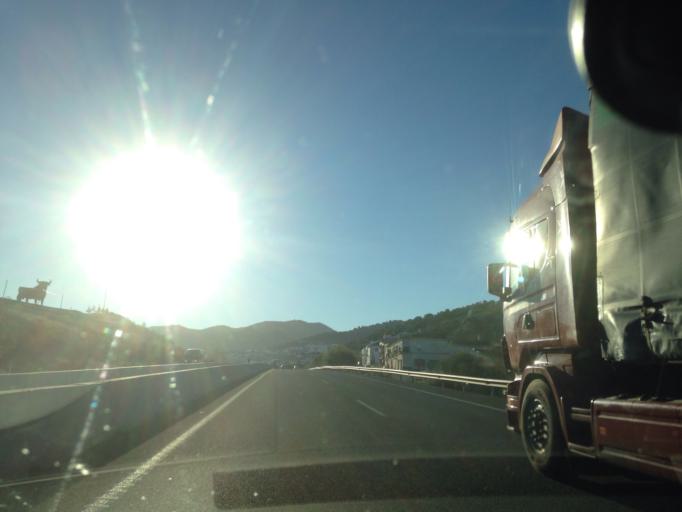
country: ES
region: Andalusia
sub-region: Provincia de Malaga
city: Casabermeja
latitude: 36.9002
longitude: -4.4377
